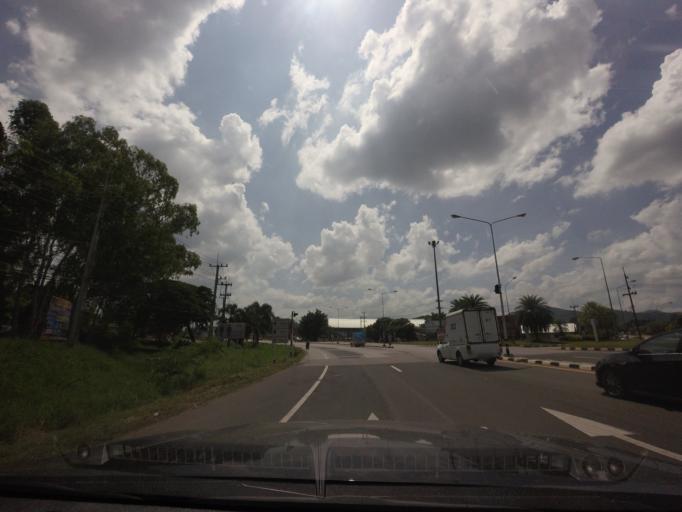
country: TH
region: Phetchabun
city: Phetchabun
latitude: 16.2648
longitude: 101.0483
